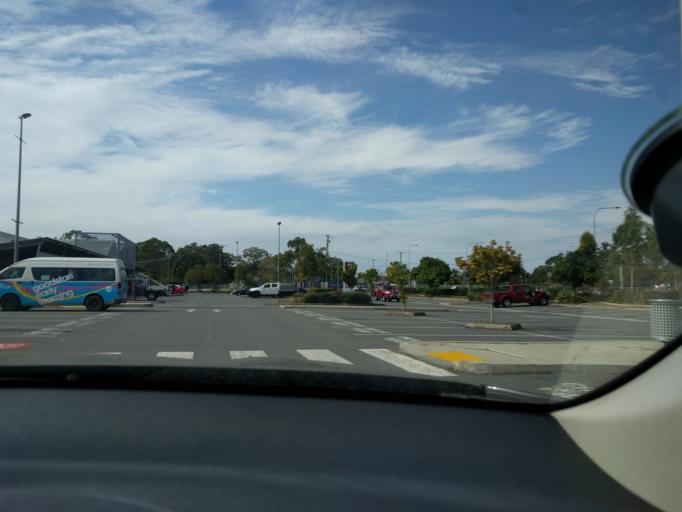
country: AU
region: Queensland
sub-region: Moreton Bay
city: Burpengary
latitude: -27.1385
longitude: 152.9810
